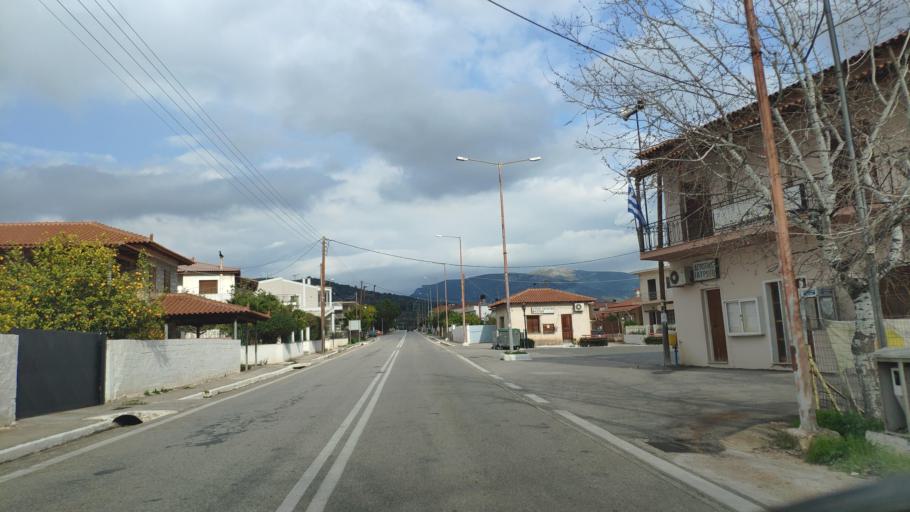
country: GR
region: Peloponnese
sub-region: Nomos Argolidos
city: Koutsopodi
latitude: 37.7226
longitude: 22.7255
